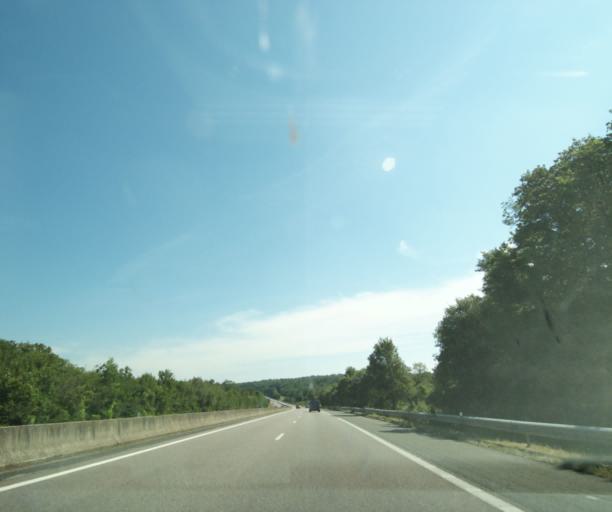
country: FR
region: Lorraine
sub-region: Departement de Meurthe-et-Moselle
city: Colombey-les-Belles
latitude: 48.4801
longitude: 5.8939
